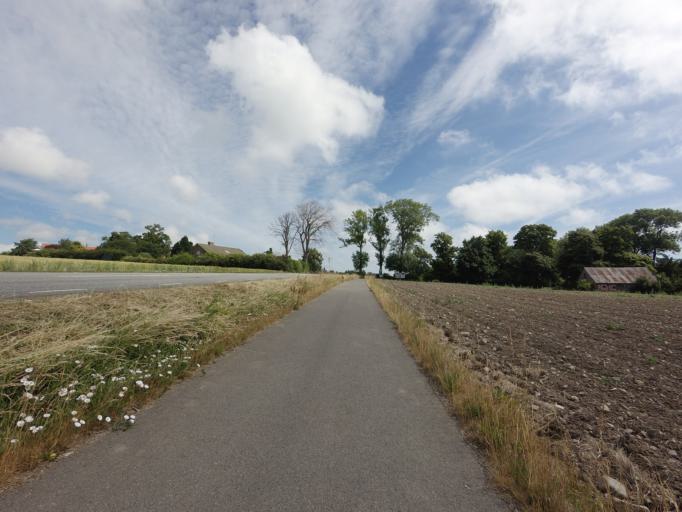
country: SE
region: Skane
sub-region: Simrishamns Kommun
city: Simrishamn
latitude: 55.5011
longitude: 14.3232
